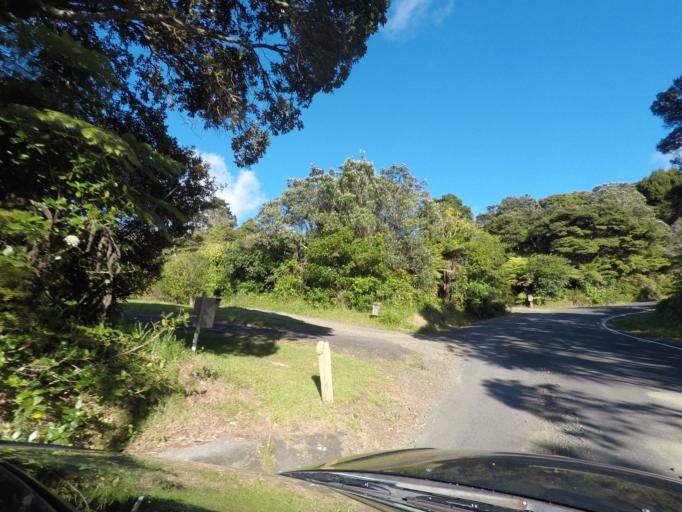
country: NZ
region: Auckland
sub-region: Auckland
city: Titirangi
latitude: -37.0091
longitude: 174.6029
